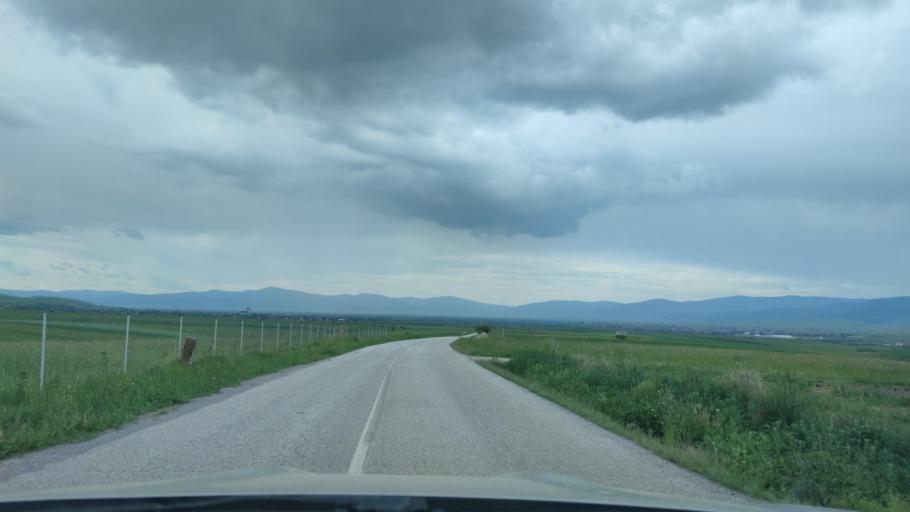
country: RO
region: Harghita
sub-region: Comuna Ditrau
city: Ditrau
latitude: 46.8406
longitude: 25.4971
